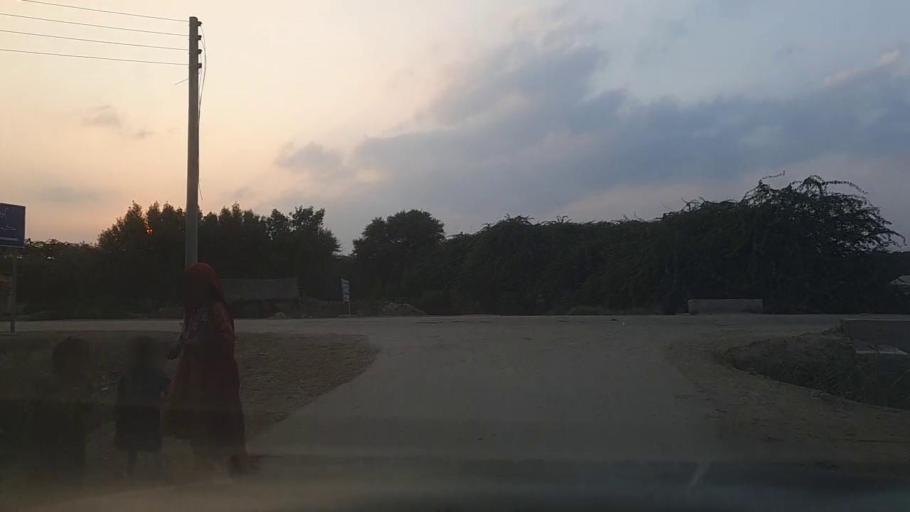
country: PK
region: Sindh
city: Jati
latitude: 24.5298
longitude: 68.3841
